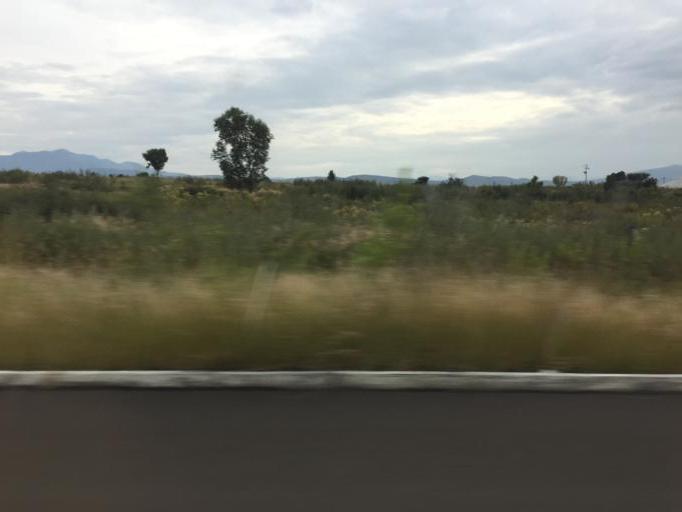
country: MX
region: Mexico
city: Huaniqueo de Morales
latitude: 19.8882
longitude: -101.5197
